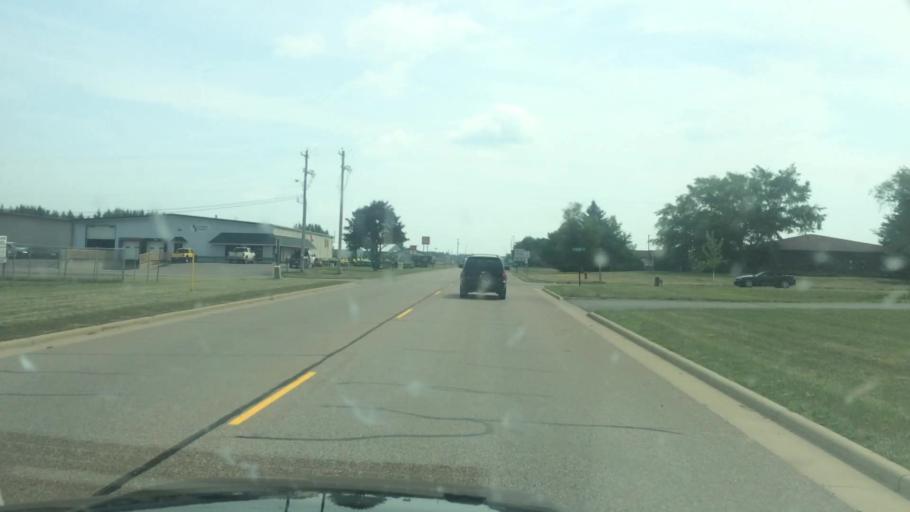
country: US
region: Wisconsin
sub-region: Langlade County
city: Antigo
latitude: 45.1621
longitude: -89.1546
